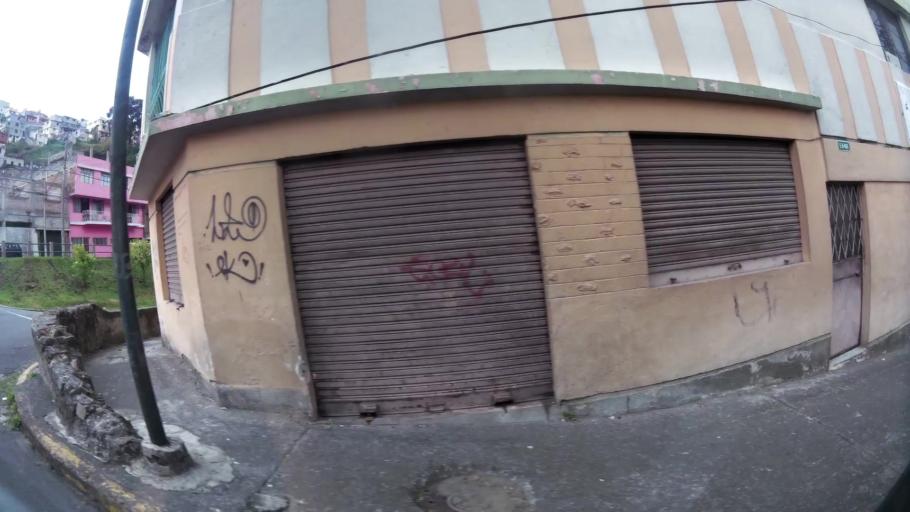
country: EC
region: Pichincha
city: Quito
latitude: -0.2478
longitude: -78.5080
